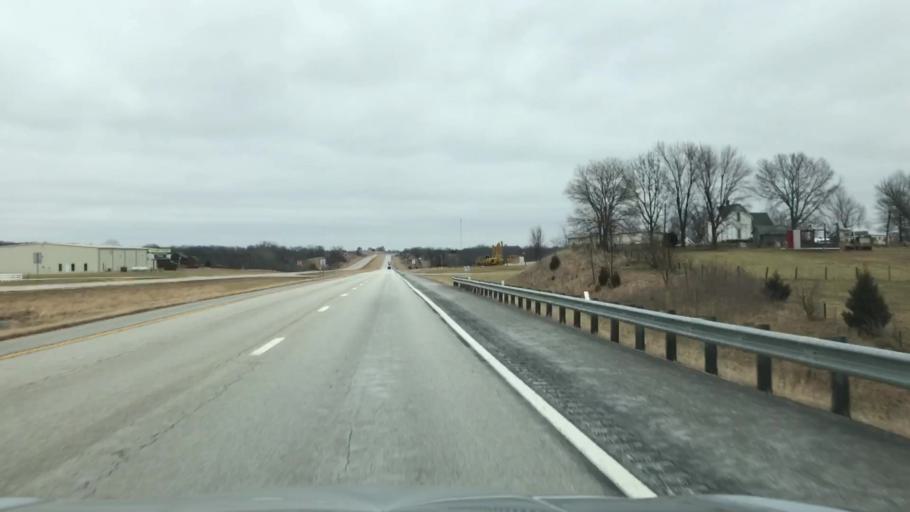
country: US
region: Missouri
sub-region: Caldwell County
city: Hamilton
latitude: 39.7493
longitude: -94.0788
